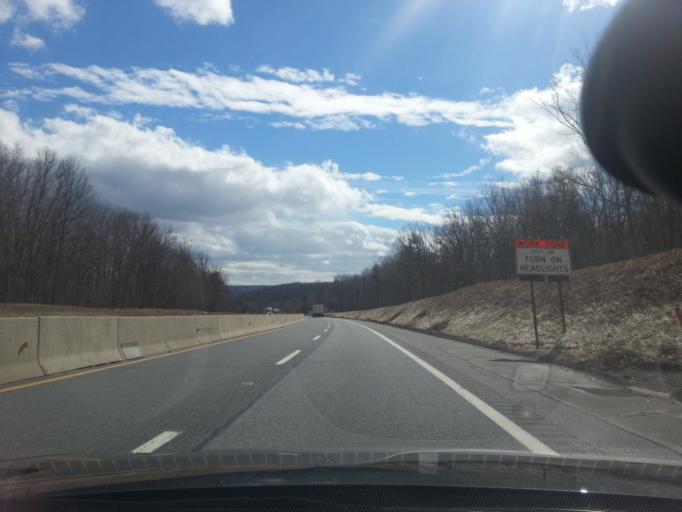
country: US
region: Pennsylvania
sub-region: Carbon County
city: Weissport East
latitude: 40.8781
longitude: -75.6574
